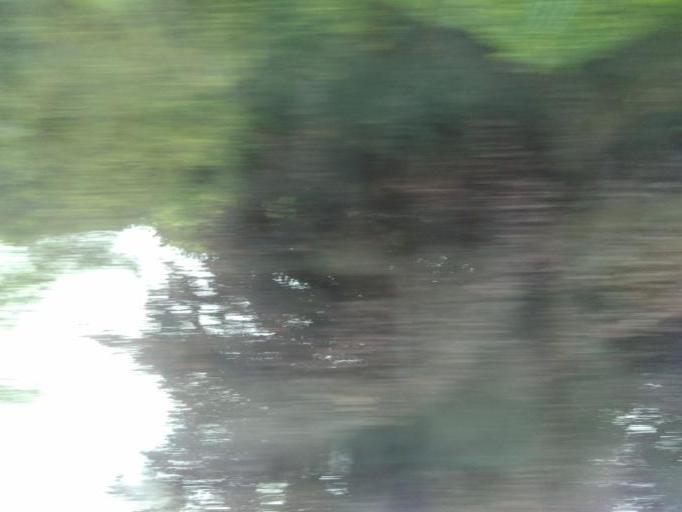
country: GB
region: Scotland
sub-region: East Lothian
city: Musselburgh
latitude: 55.9441
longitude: -3.0907
